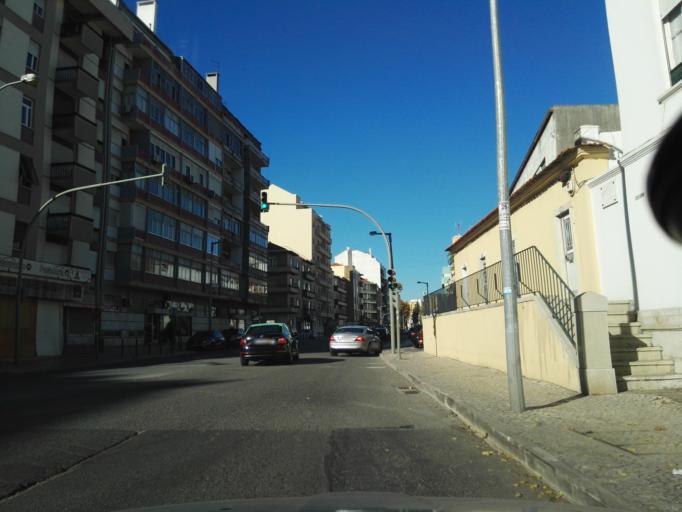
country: PT
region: Lisbon
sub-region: Odivelas
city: Olival do Basto
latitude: 38.7627
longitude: -9.1566
